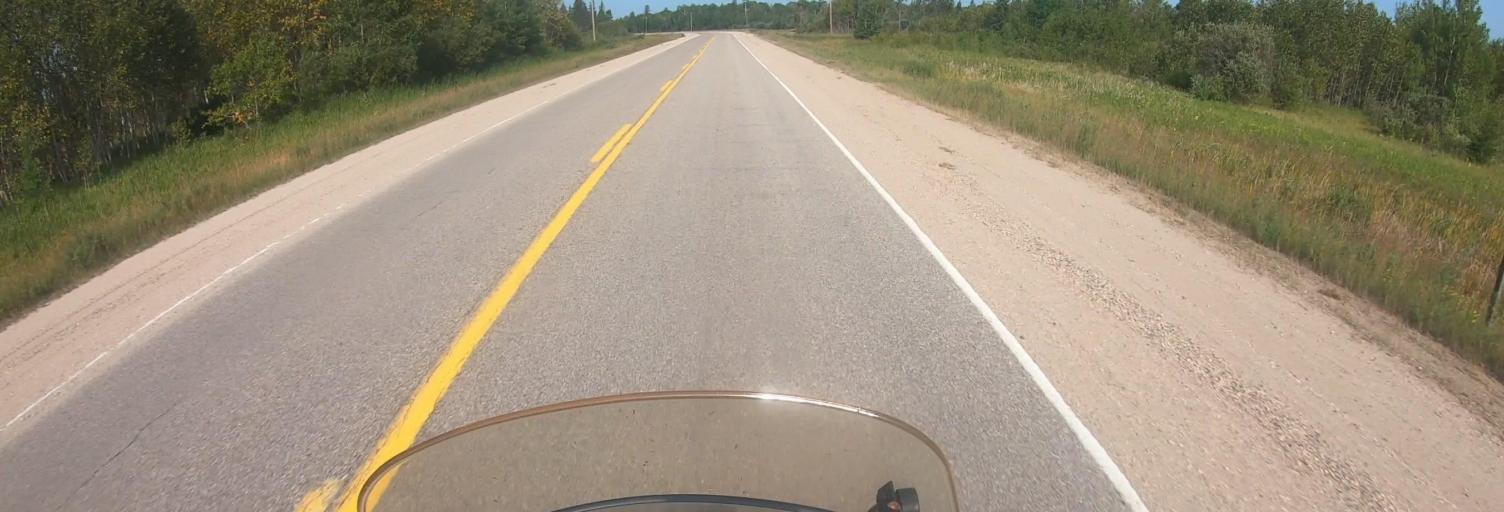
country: US
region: Minnesota
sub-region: Roseau County
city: Warroad
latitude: 49.0148
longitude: -95.4054
